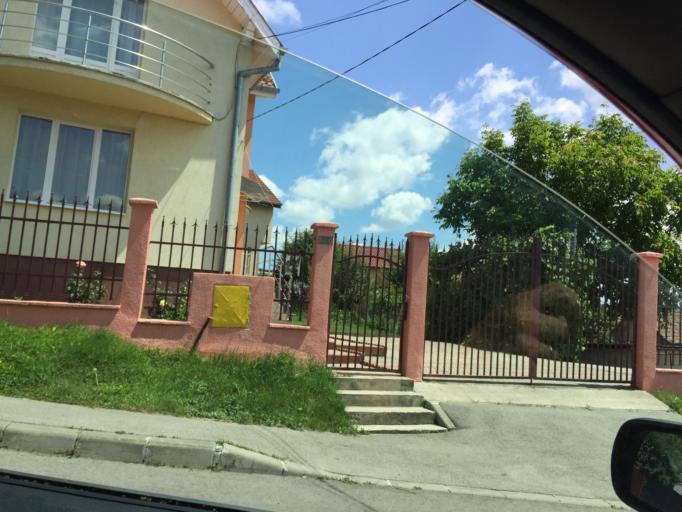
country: RO
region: Cluj
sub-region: Municipiul Cluj-Napoca
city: Cluj-Napoca
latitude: 46.7912
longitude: 23.5795
